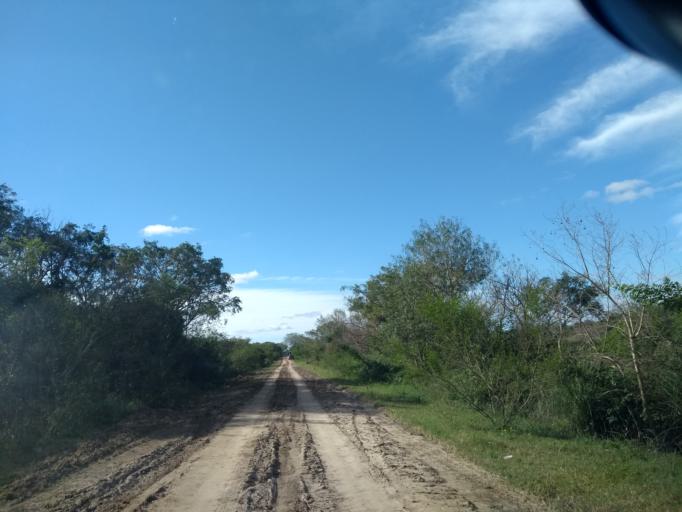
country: AR
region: Chaco
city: Margarita Belen
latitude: -27.2807
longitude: -58.9242
